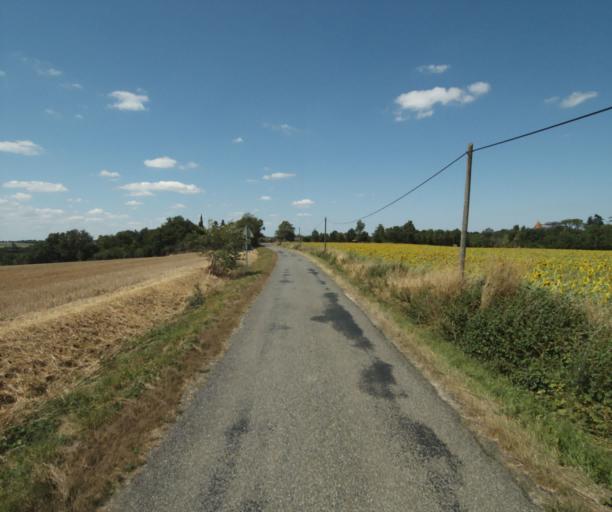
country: FR
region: Midi-Pyrenees
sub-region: Departement de la Haute-Garonne
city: Saint-Felix-Lauragais
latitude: 43.4749
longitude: 1.8603
